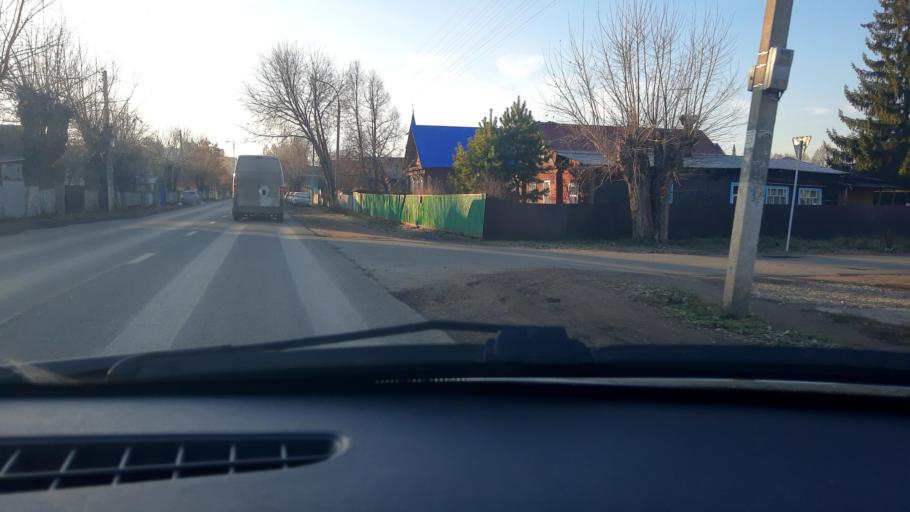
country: RU
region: Bashkortostan
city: Avdon
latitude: 54.7061
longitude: 55.8203
